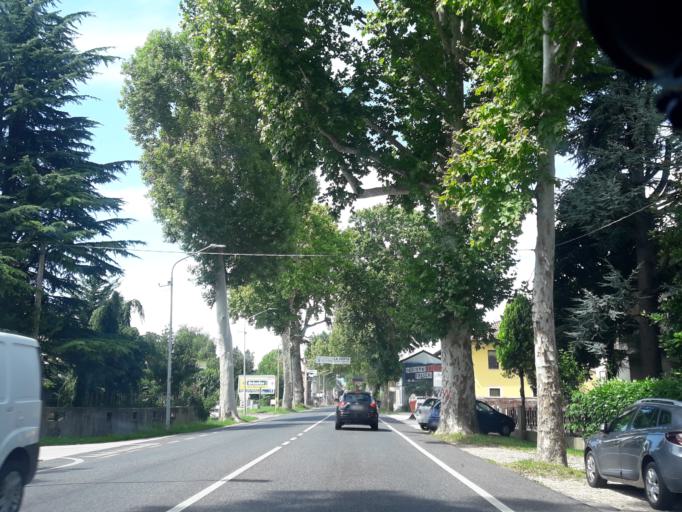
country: IT
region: Friuli Venezia Giulia
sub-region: Provincia di Udine
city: Udine
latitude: 46.0499
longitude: 13.2485
